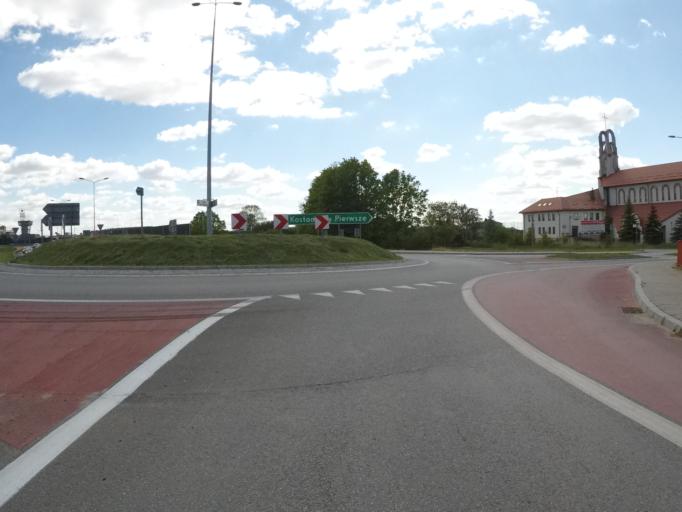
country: PL
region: Swietokrzyskie
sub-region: Powiat kielecki
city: Kostomloty Pierwsze
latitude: 50.9068
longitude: 20.5882
